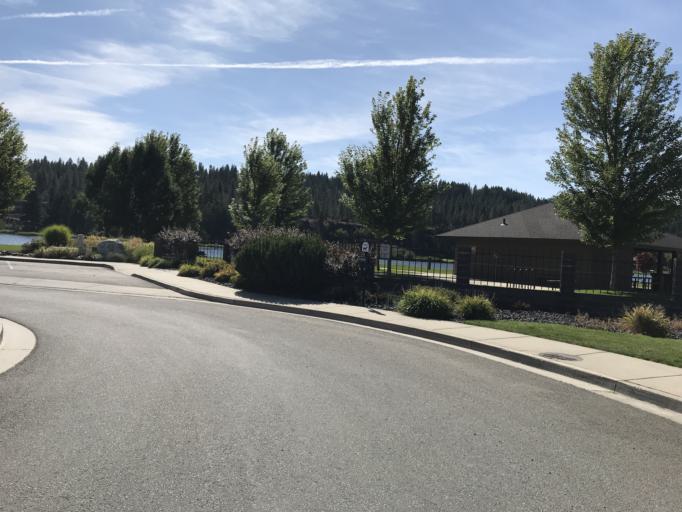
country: US
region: Idaho
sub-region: Kootenai County
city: Coeur d'Alene
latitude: 47.7010
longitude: -116.8449
